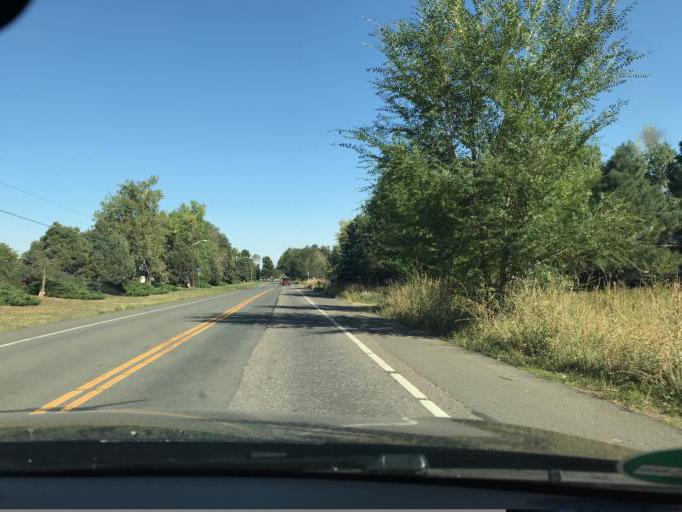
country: US
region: Colorado
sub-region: Boulder County
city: Boulder
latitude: 40.0547
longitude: -105.2707
